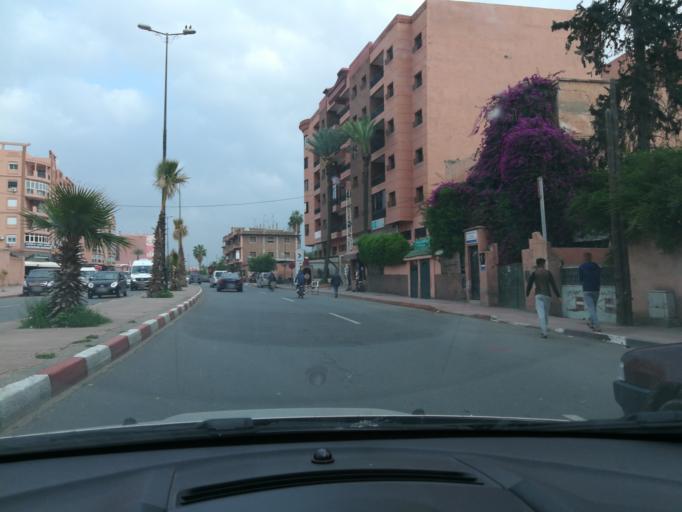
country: MA
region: Marrakech-Tensift-Al Haouz
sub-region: Marrakech
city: Marrakesh
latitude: 31.6379
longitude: -8.0032
